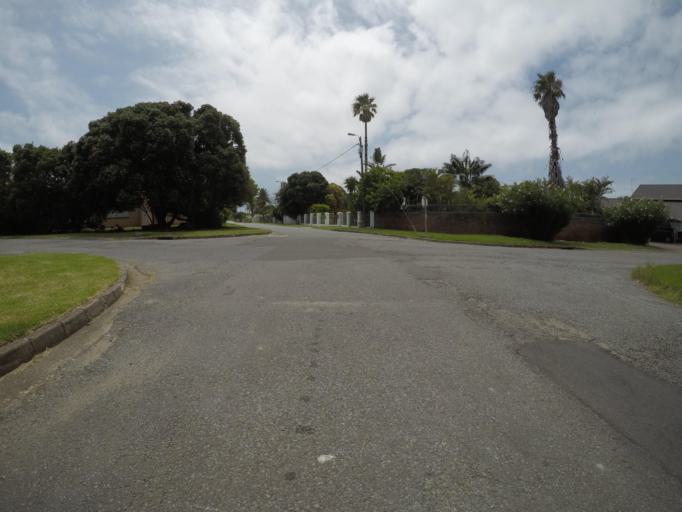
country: ZA
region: Eastern Cape
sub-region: Buffalo City Metropolitan Municipality
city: East London
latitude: -32.9479
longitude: 28.0202
